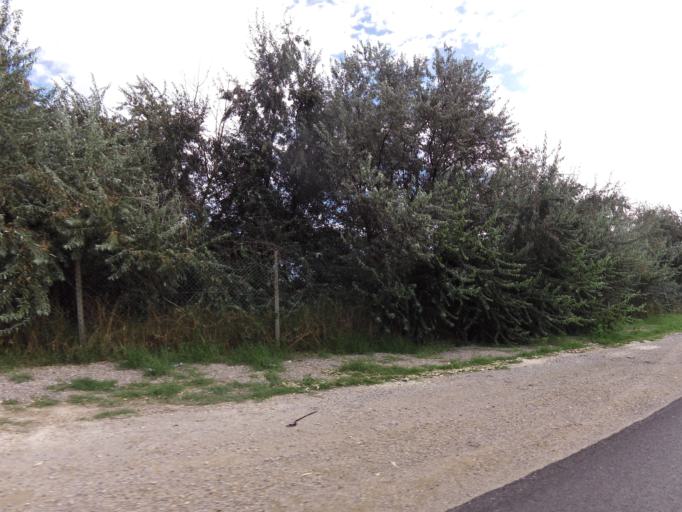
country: FR
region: Languedoc-Roussillon
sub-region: Departement du Gard
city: Le Grau-du-Roi
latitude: 43.5144
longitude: 4.1495
